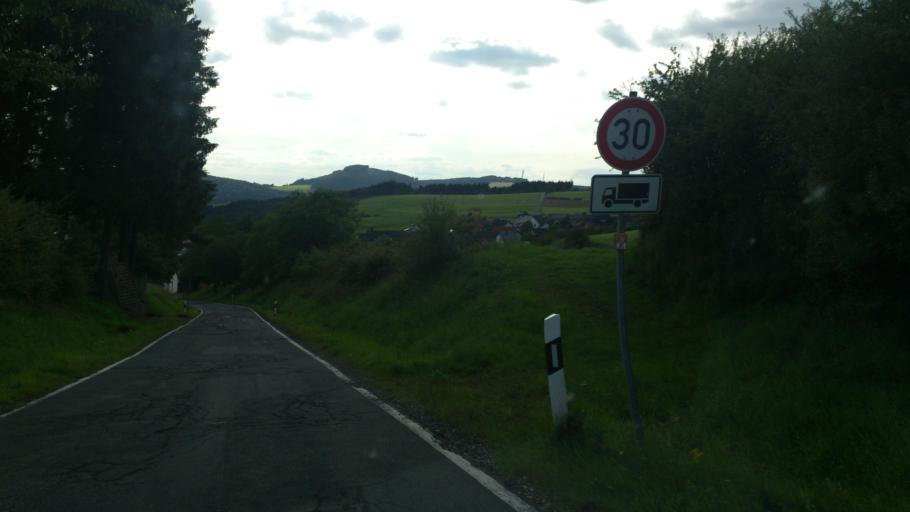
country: DE
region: Rheinland-Pfalz
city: Dreis-Bruck
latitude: 50.2769
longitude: 6.8143
